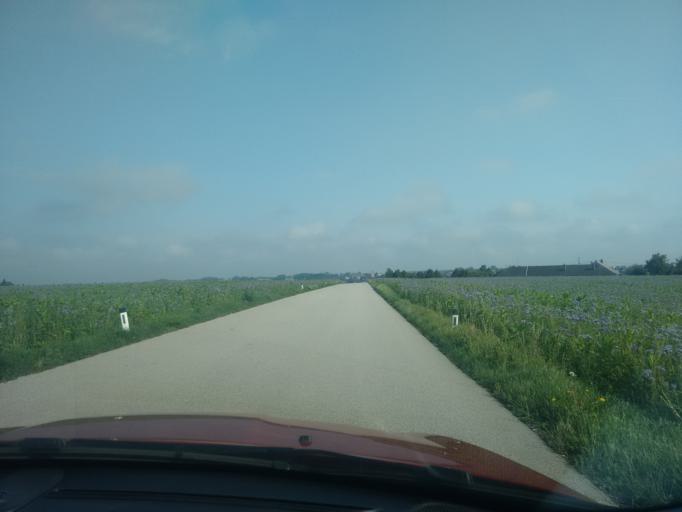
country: AT
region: Upper Austria
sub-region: Wels-Land
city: Steinhaus
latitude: 48.1099
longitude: 14.0070
